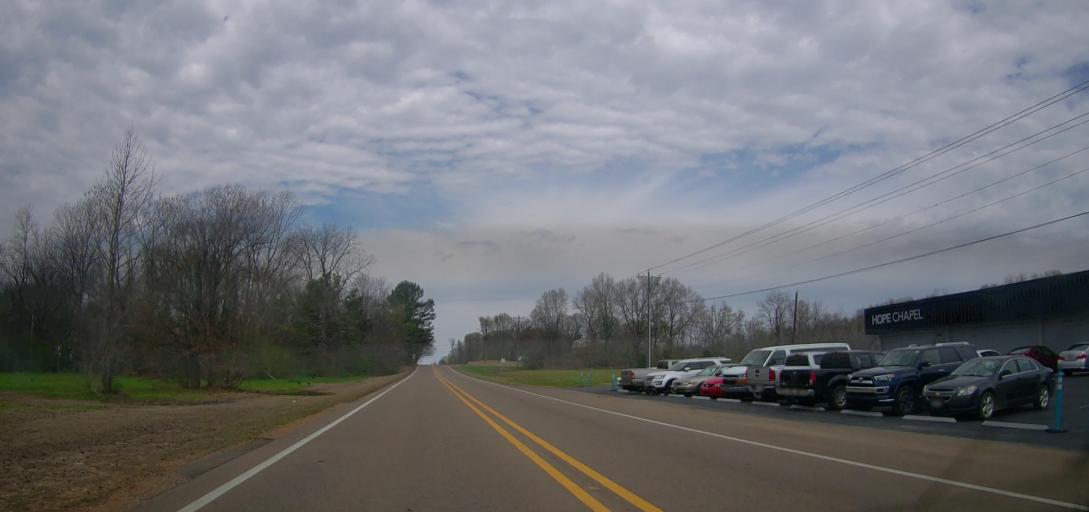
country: US
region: Mississippi
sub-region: De Soto County
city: Olive Branch
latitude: 34.9703
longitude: -89.8374
